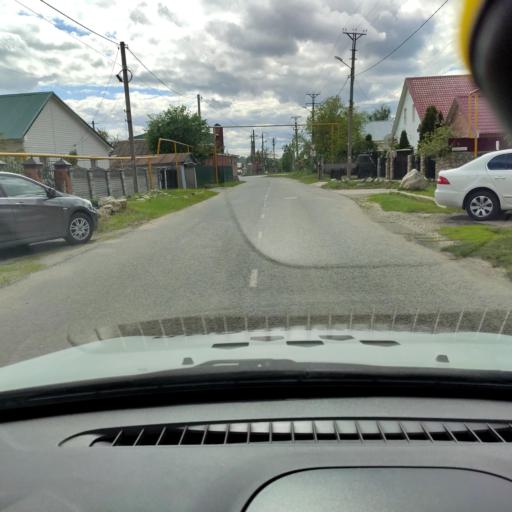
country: RU
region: Samara
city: Zhigulevsk
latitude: 53.4669
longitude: 49.6386
